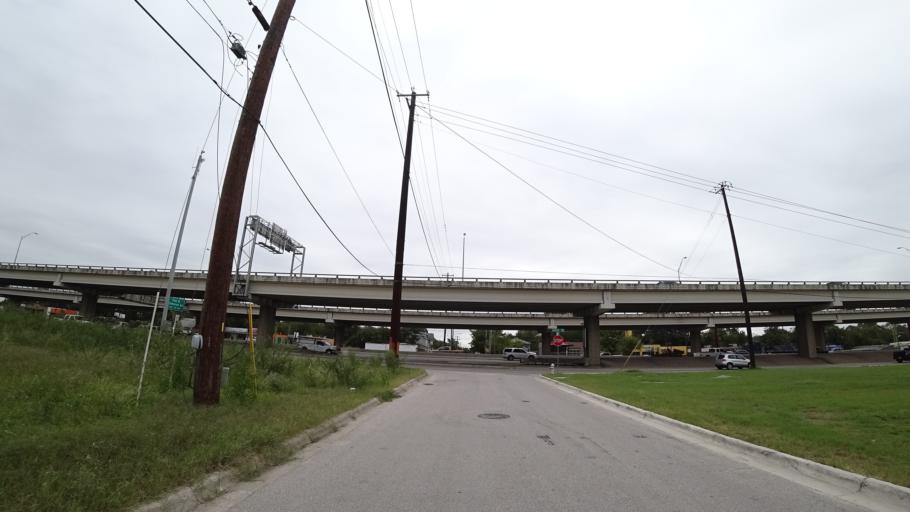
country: US
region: Texas
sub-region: Travis County
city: Austin
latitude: 30.2931
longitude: -97.7213
